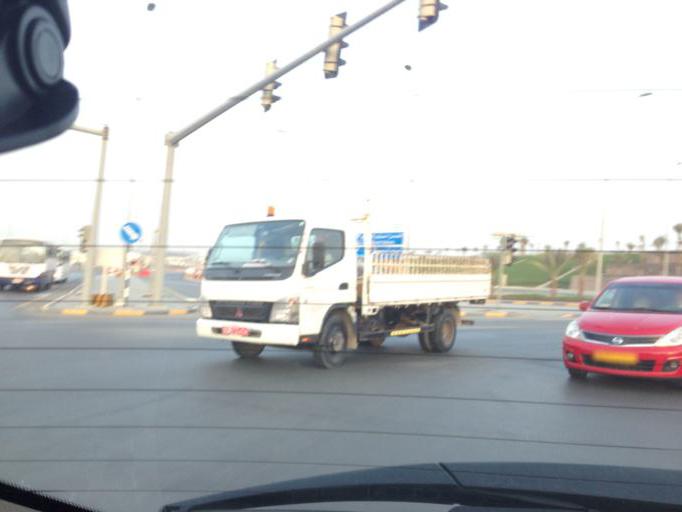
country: OM
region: Muhafazat Masqat
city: Bawshar
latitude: 23.6016
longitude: 58.3120
